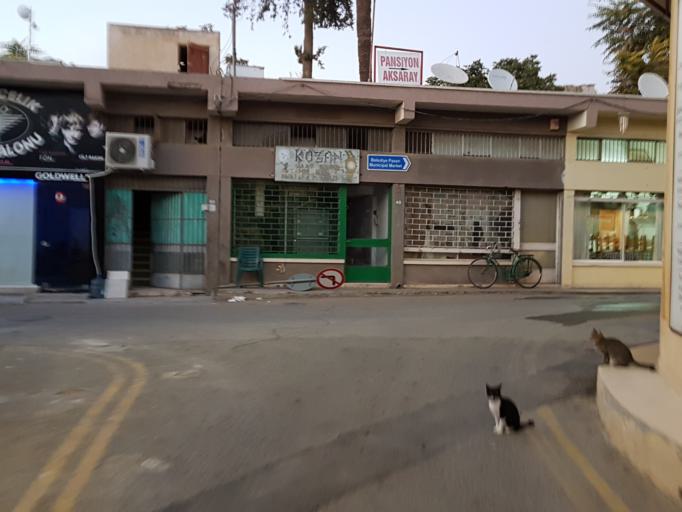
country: CY
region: Lefkosia
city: Nicosia
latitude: 35.1772
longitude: 33.3628
